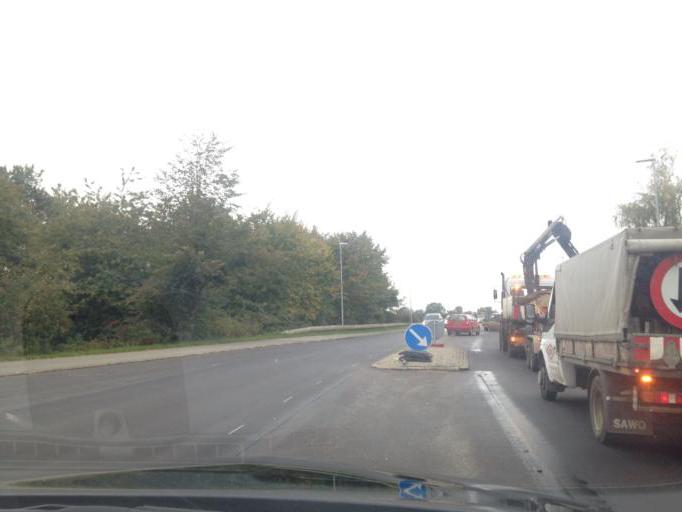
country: DK
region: South Denmark
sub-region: Kolding Kommune
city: Kolding
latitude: 55.4597
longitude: 9.4737
